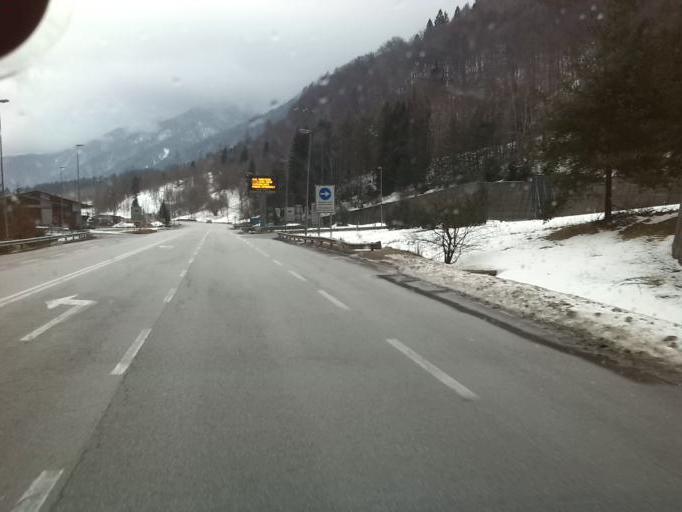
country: IT
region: Friuli Venezia Giulia
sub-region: Provincia di Udine
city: Pontebba
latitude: 46.5098
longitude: 13.3394
